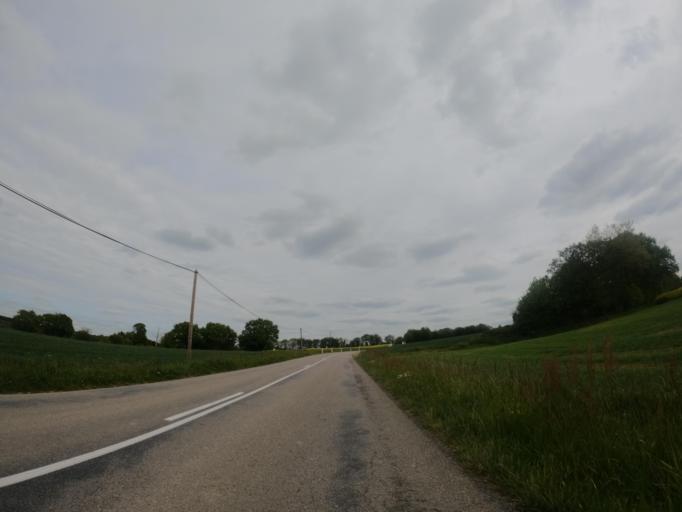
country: FR
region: Pays de la Loire
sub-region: Departement de la Loire-Atlantique
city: Chateaubriant
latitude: 47.7366
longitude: -1.4216
